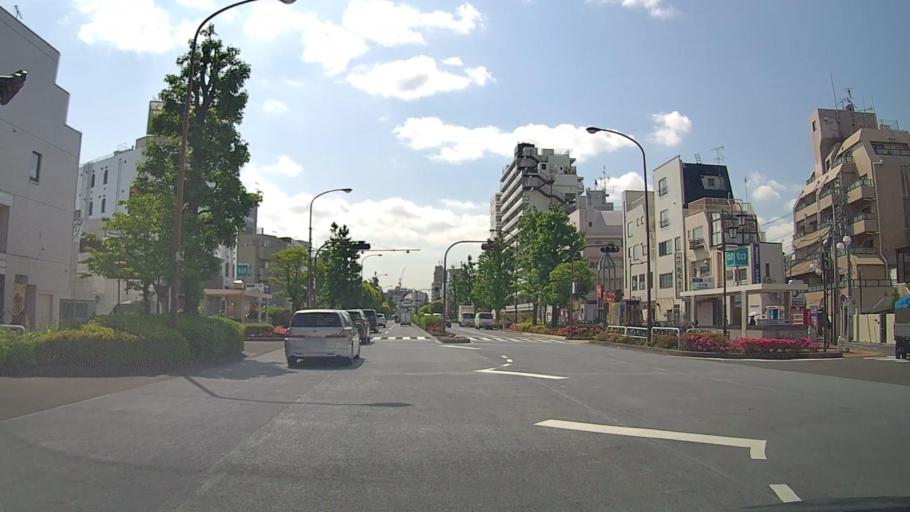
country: JP
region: Tokyo
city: Tokyo
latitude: 35.7381
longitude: 139.6897
